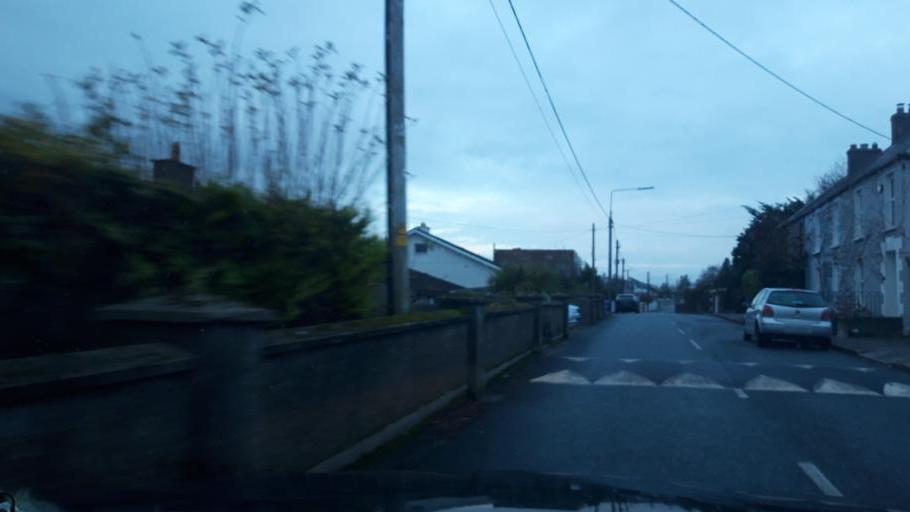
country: IE
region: Leinster
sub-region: Kilkenny
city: Kilkenny
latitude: 52.6600
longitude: -7.2534
